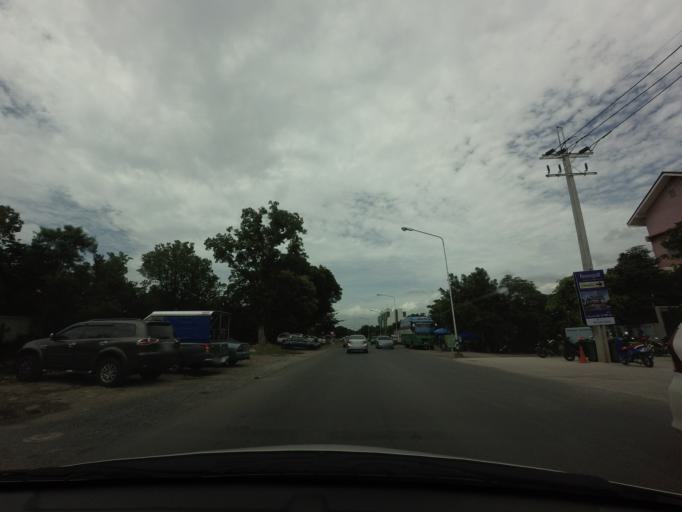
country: TH
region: Bangkok
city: Lak Si
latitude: 13.8572
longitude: 100.5769
